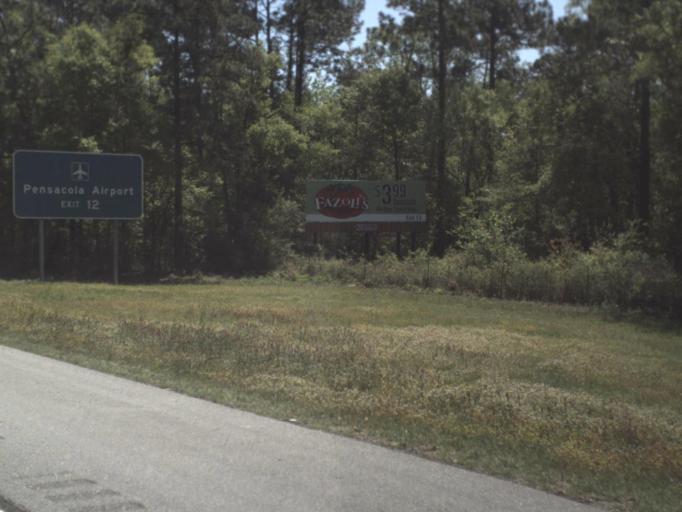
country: US
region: Florida
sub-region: Escambia County
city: Ensley
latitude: 30.5037
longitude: -87.2471
